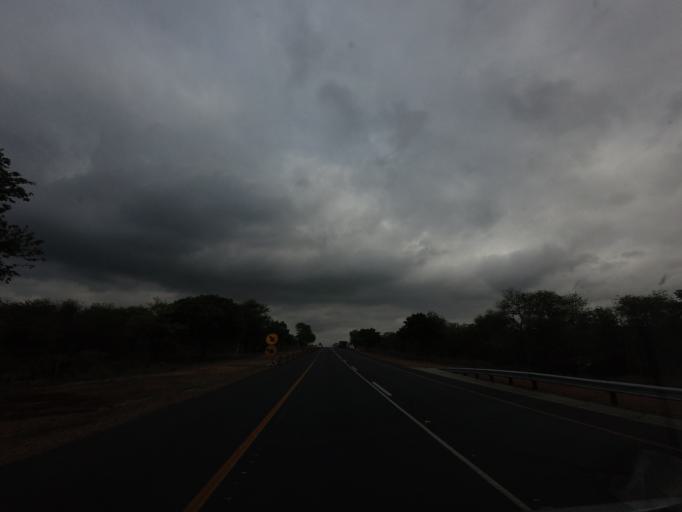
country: ZA
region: Mpumalanga
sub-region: Ehlanzeni District
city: Komatipoort
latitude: -25.4406
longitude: 31.7453
